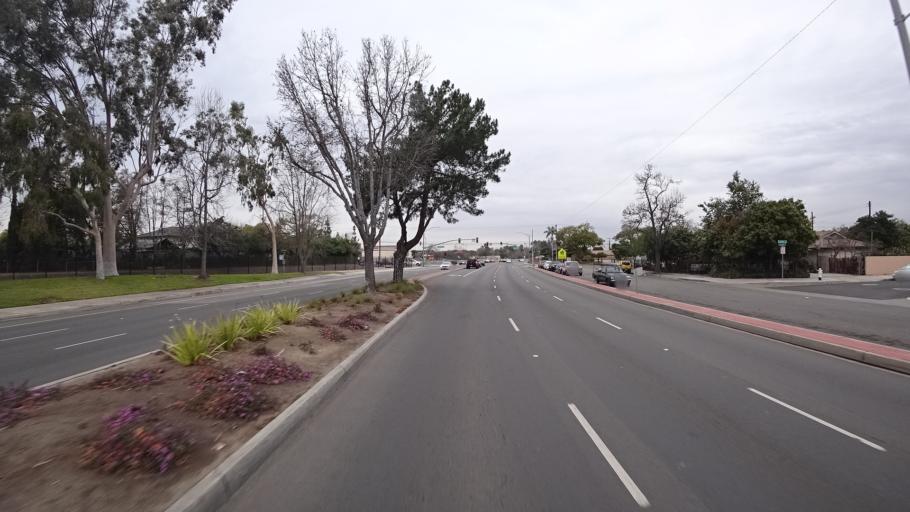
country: US
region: California
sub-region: Orange County
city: Fountain Valley
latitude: 33.7192
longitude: -117.9085
